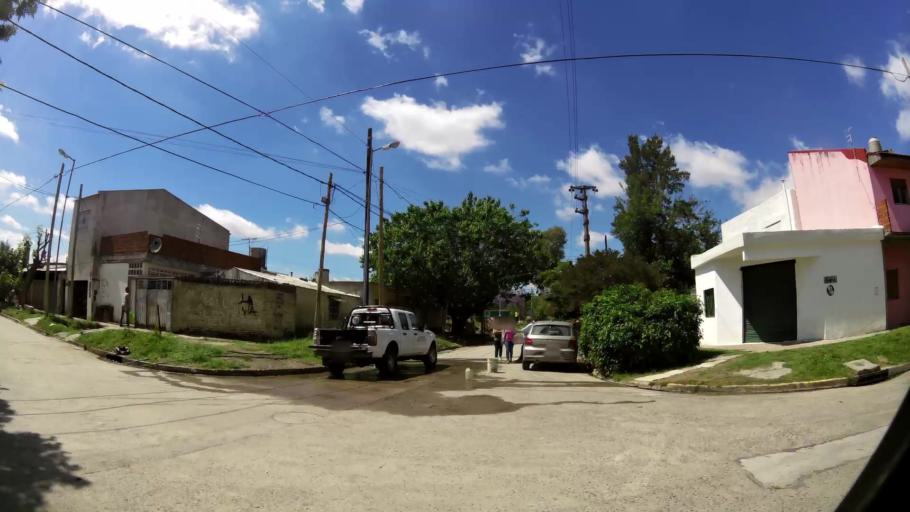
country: AR
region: Buenos Aires
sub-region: Partido de Lanus
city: Lanus
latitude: -34.6940
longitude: -58.4277
